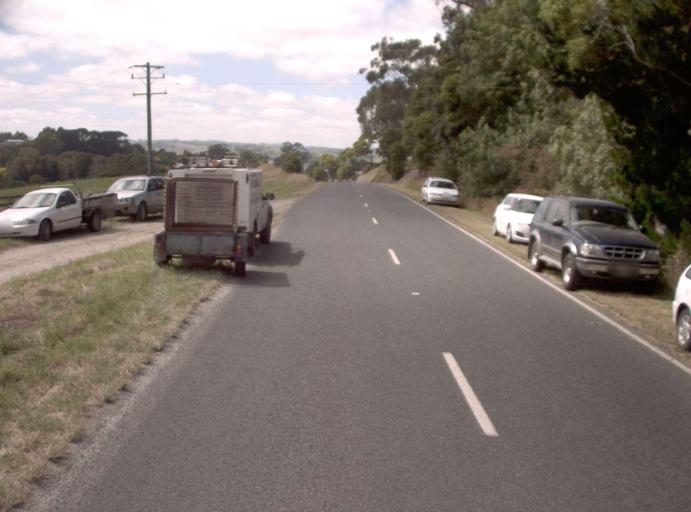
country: AU
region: Victoria
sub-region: Cardinia
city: Bunyip
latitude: -38.3423
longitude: 145.7382
